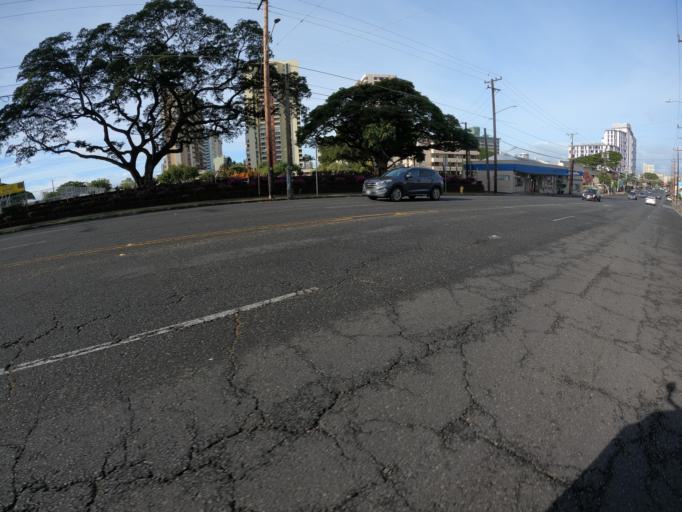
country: US
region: Hawaii
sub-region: Honolulu County
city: Honolulu
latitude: 21.2904
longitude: -157.8192
